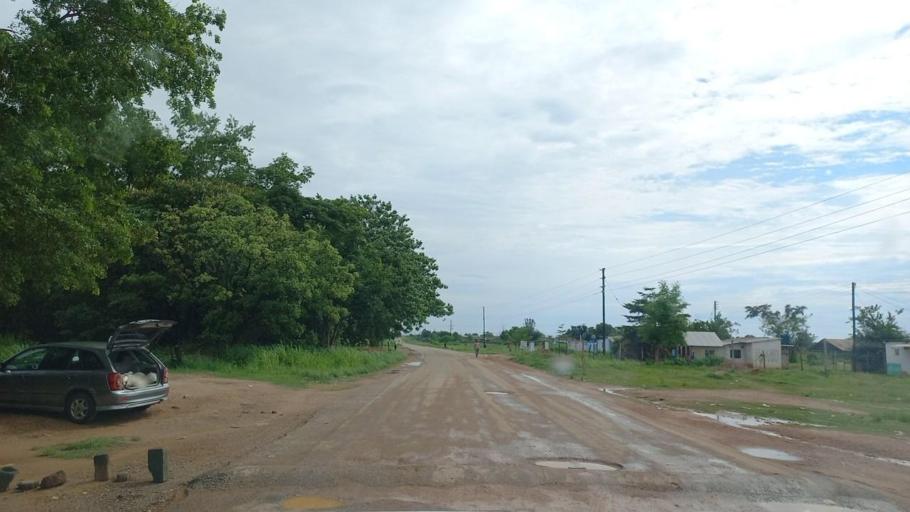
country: ZM
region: Copperbelt
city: Kitwe
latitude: -12.8792
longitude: 28.3241
